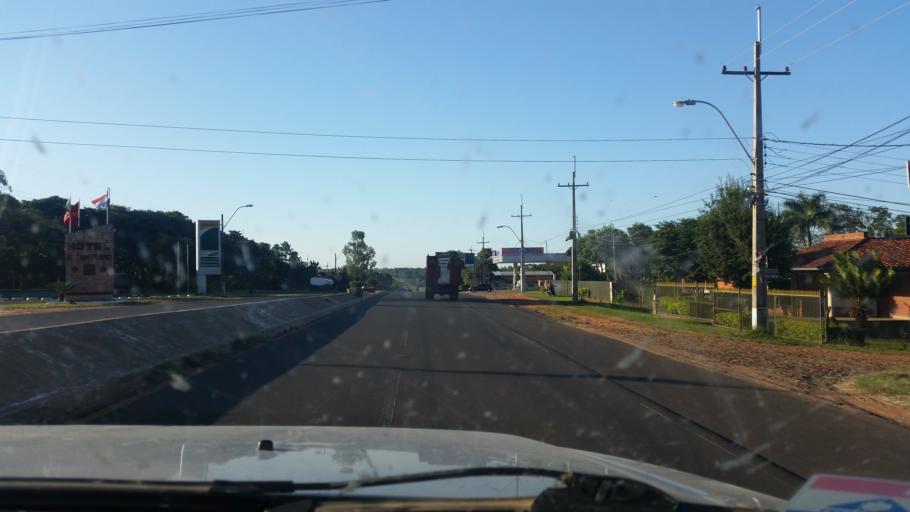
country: PY
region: Misiones
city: Santa Maria
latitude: -26.8783
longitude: -57.0321
